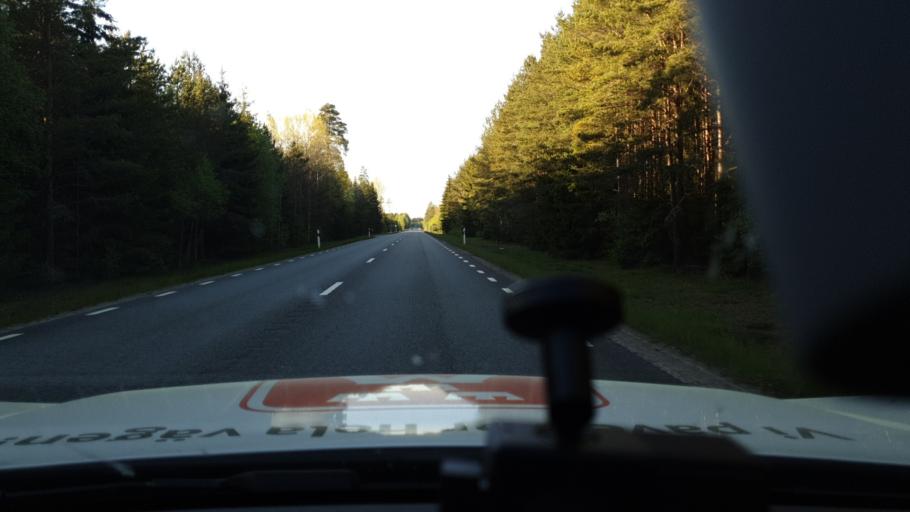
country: SE
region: Joenkoeping
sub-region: Eksjo Kommun
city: Eksjoe
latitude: 57.6228
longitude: 14.9694
